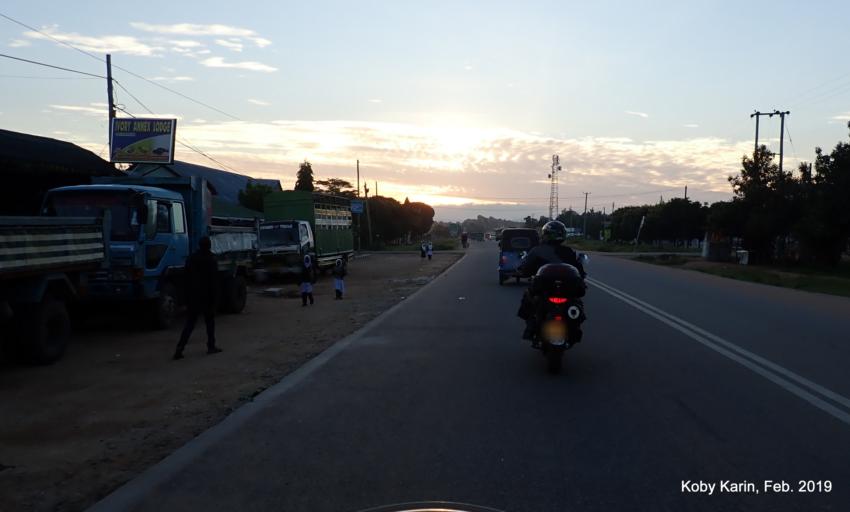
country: TZ
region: Singida
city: Singida
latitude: -4.8202
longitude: 34.7599
